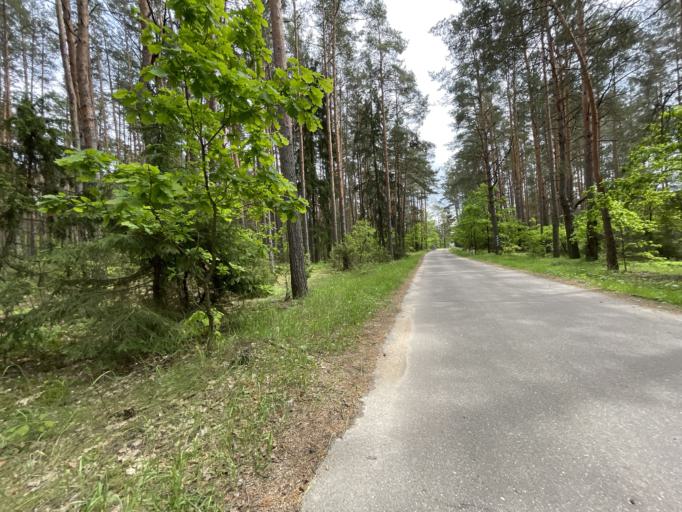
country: BY
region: Minsk
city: Stowbtsy
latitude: 53.4273
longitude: 26.8123
